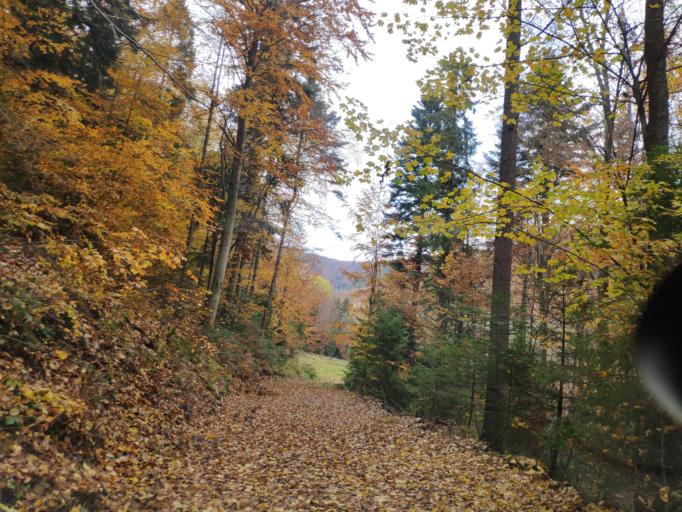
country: SK
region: Kosicky
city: Medzev
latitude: 48.7619
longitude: 20.9697
